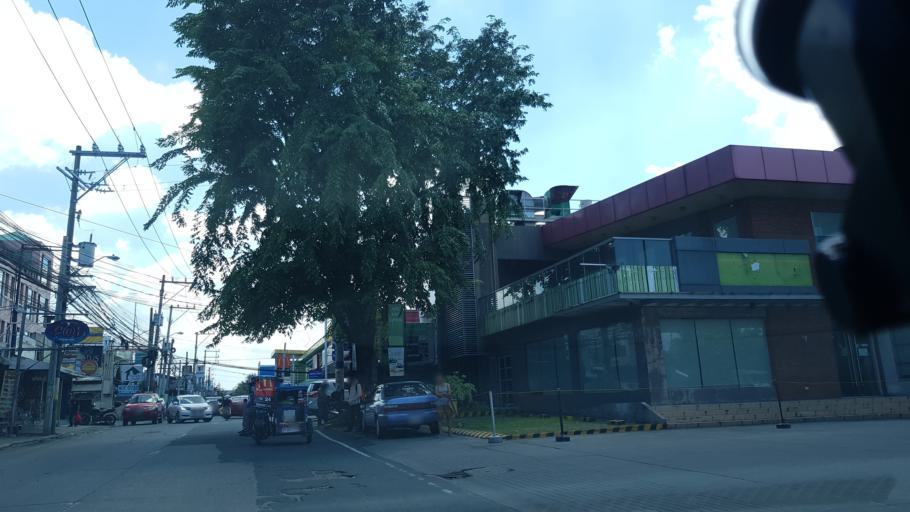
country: PH
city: Sambayanihan People's Village
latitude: 14.4483
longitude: 121.0295
